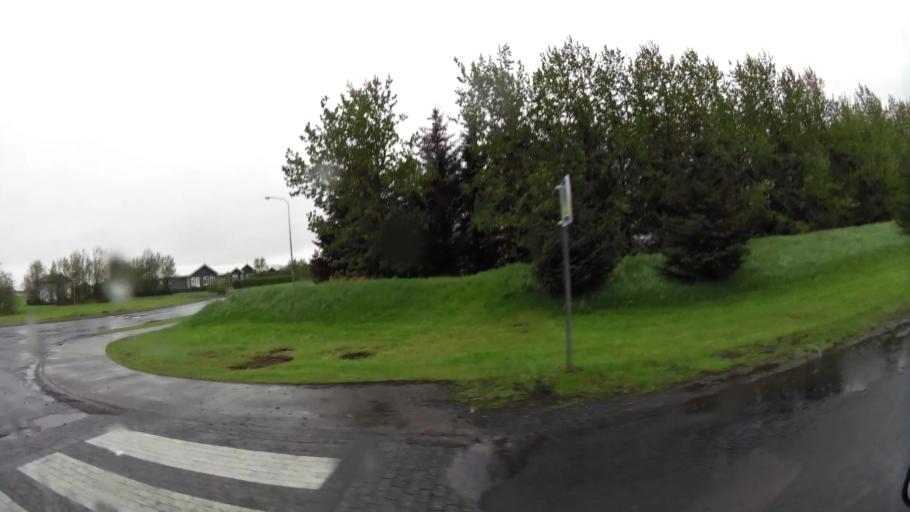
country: IS
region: South
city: Selfoss
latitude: 63.9340
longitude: -20.9791
